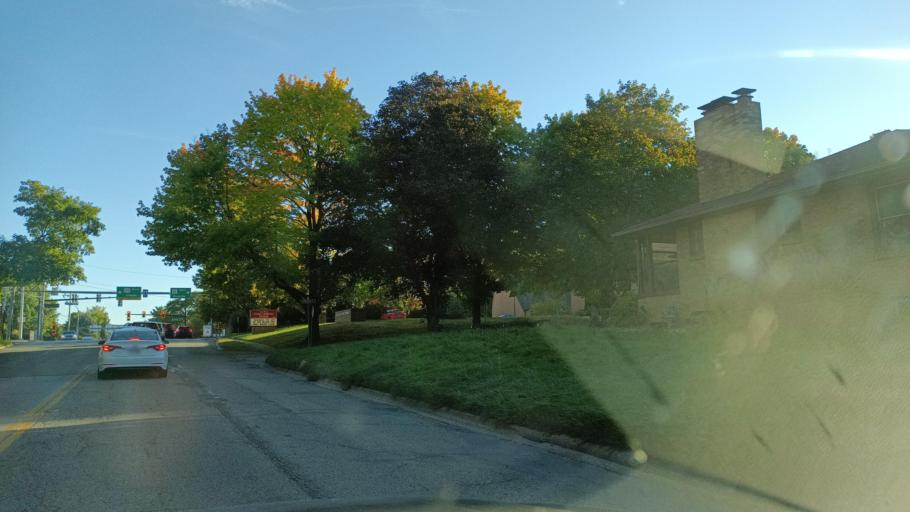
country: US
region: Illinois
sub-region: Champaign County
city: Champaign
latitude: 40.1139
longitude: -88.2579
